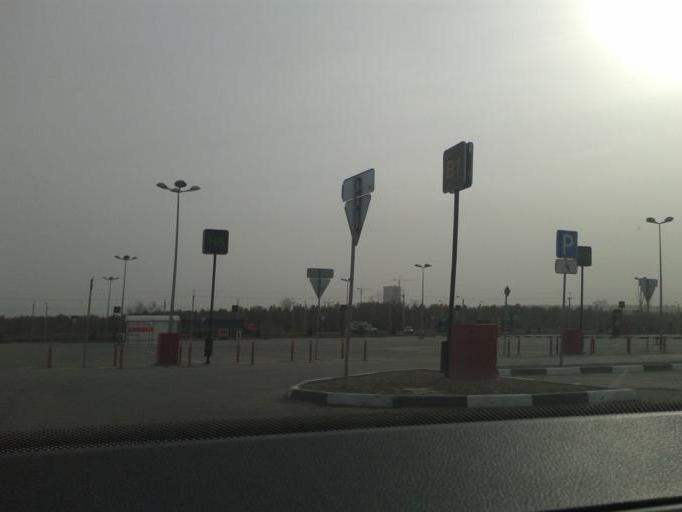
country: RU
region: Volgograd
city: Volgograd
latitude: 48.6348
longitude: 44.4343
